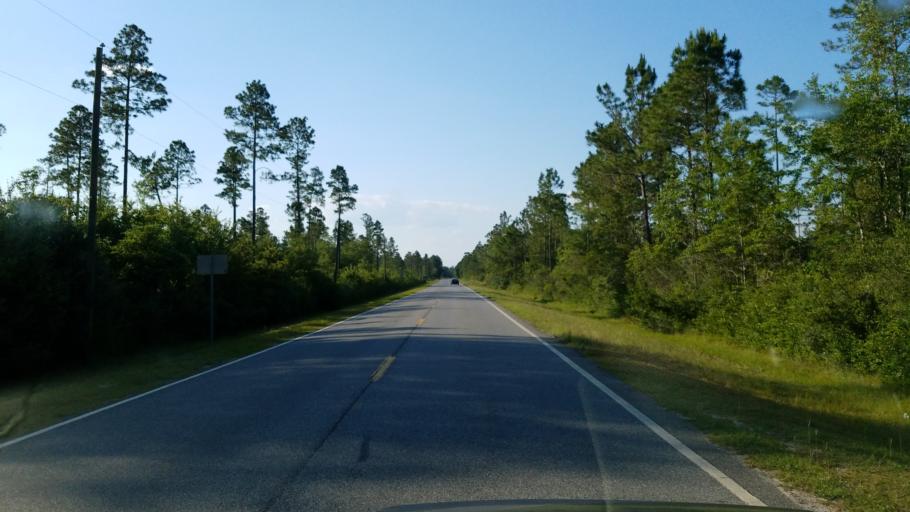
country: US
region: Georgia
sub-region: Lanier County
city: Lakeland
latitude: 30.9154
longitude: -83.0794
